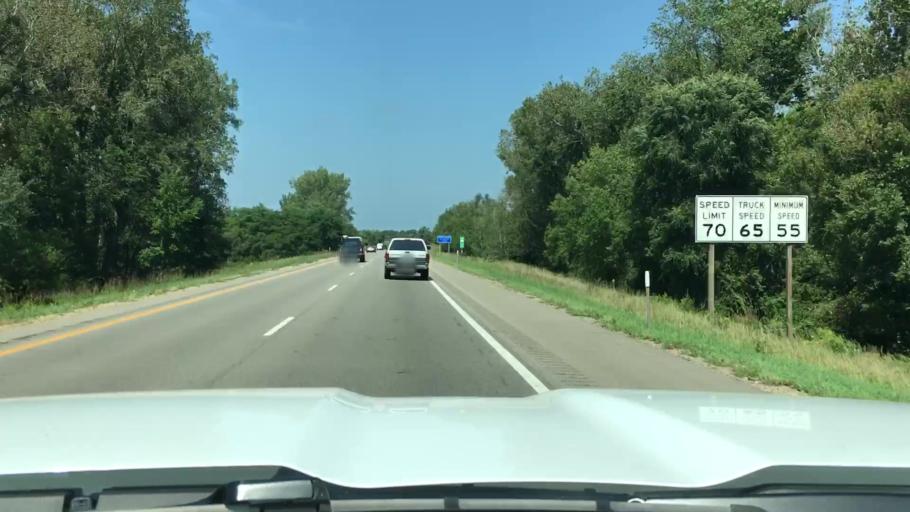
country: US
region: Michigan
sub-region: Kalamazoo County
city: Schoolcraft
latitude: 42.1503
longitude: -85.6399
